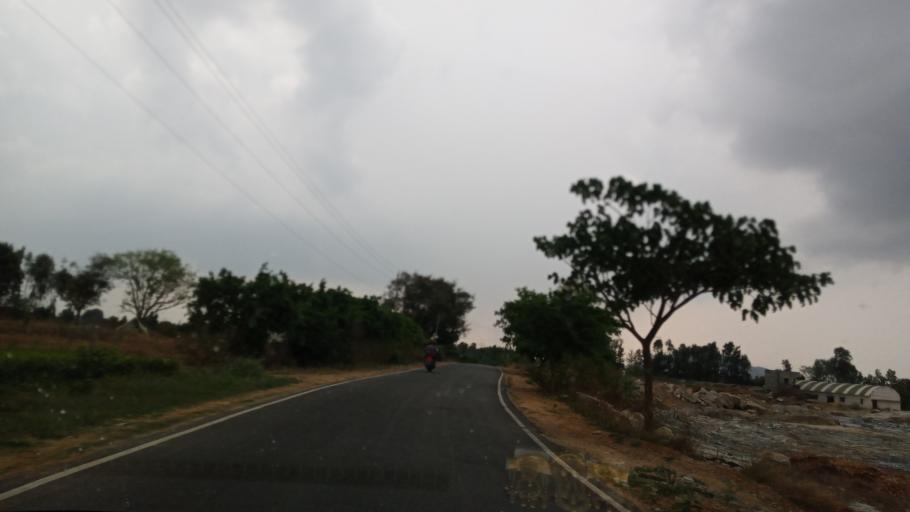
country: IN
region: Karnataka
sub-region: Kolar
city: Mulbagal
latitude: 13.1320
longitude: 78.3559
